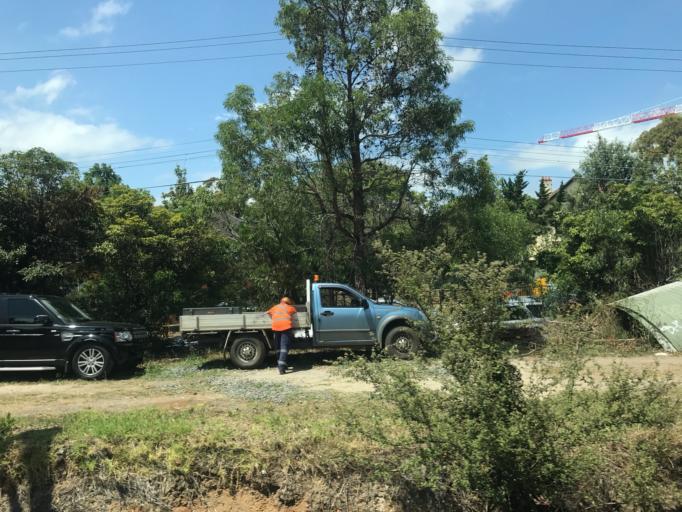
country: AU
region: New South Wales
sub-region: Ku-ring-gai
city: Lindfield
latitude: -33.7861
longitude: 151.1794
